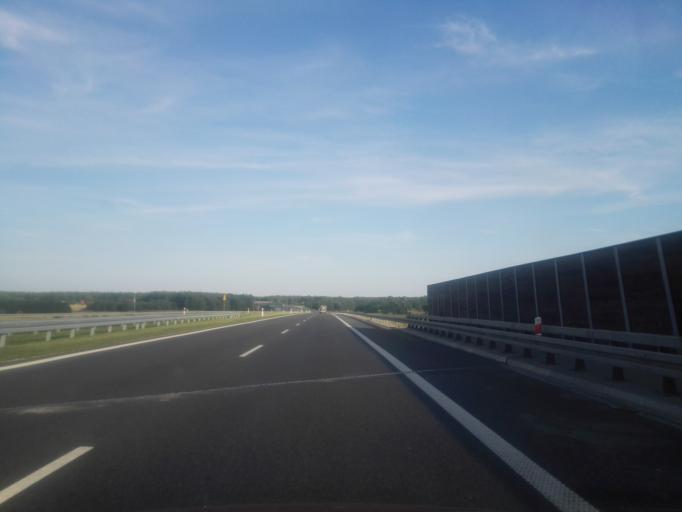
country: PL
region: Lodz Voivodeship
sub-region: Powiat wieruszowski
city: Wieruszow
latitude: 51.3177
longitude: 18.1651
